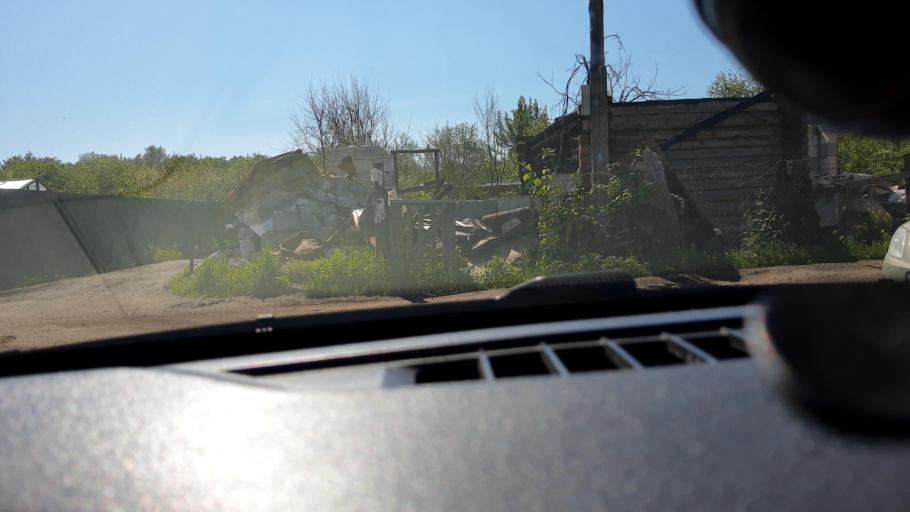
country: RU
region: Nizjnij Novgorod
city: Gorbatovka
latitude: 56.2781
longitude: 43.7870
